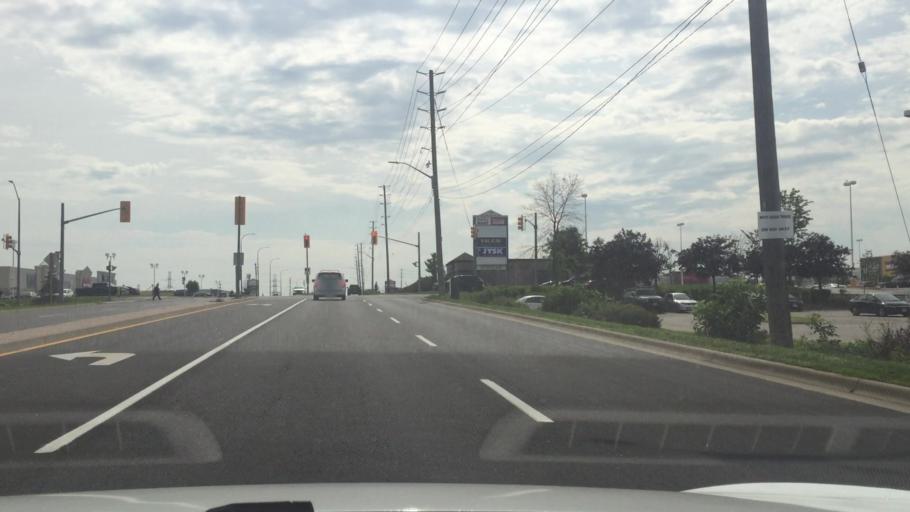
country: CA
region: Ontario
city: Oshawa
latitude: 43.8680
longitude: -78.8983
